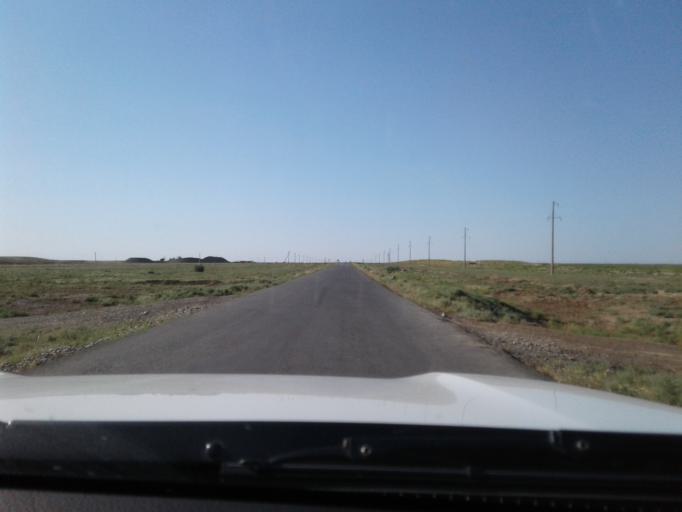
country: IR
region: Razavi Khorasan
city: Kalat-e Naderi
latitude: 37.1698
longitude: 60.0468
